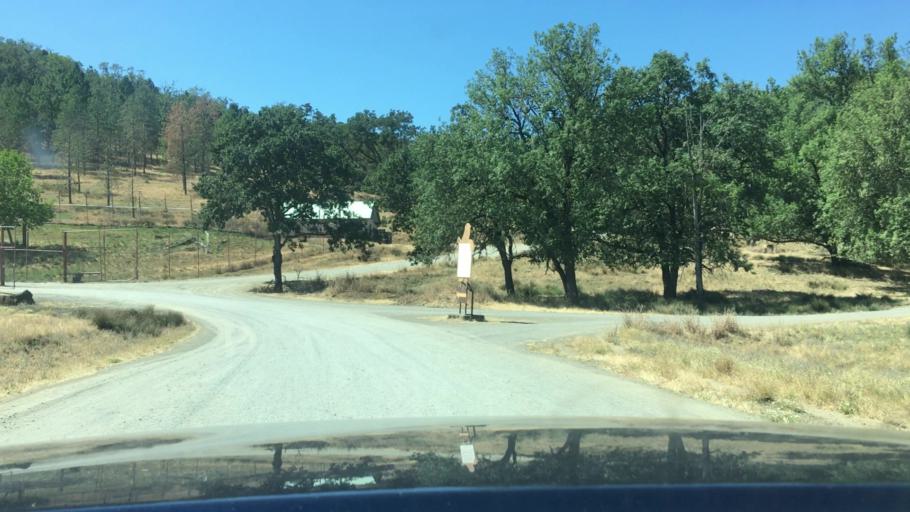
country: US
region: Oregon
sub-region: Douglas County
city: Winston
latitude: 43.1324
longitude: -123.4365
